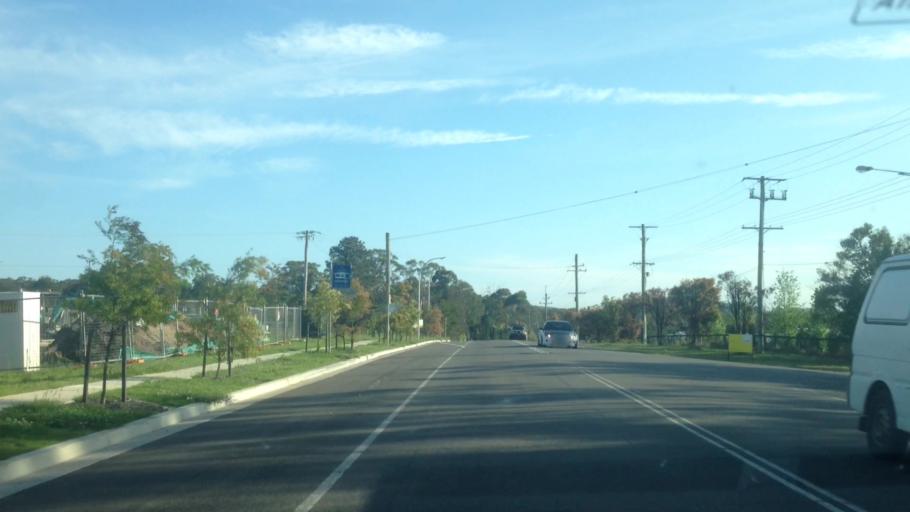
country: AU
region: New South Wales
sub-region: Lake Macquarie Shire
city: Dora Creek
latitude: -33.1049
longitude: 151.4771
